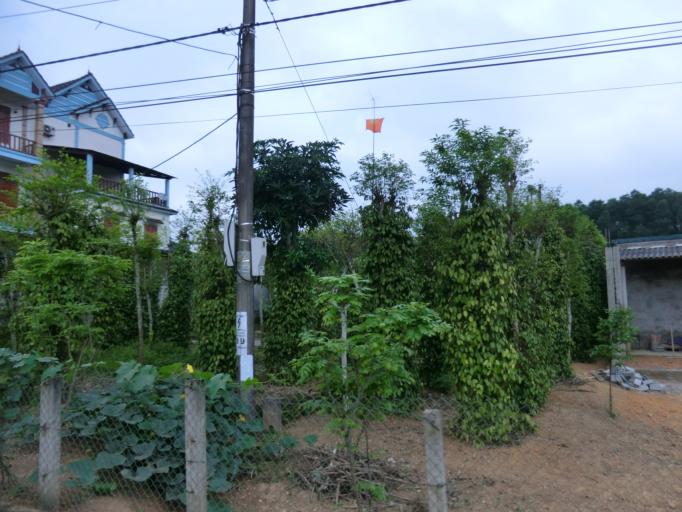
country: VN
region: Quang Binh
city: Hoan Lao
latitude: 17.6301
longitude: 106.4298
